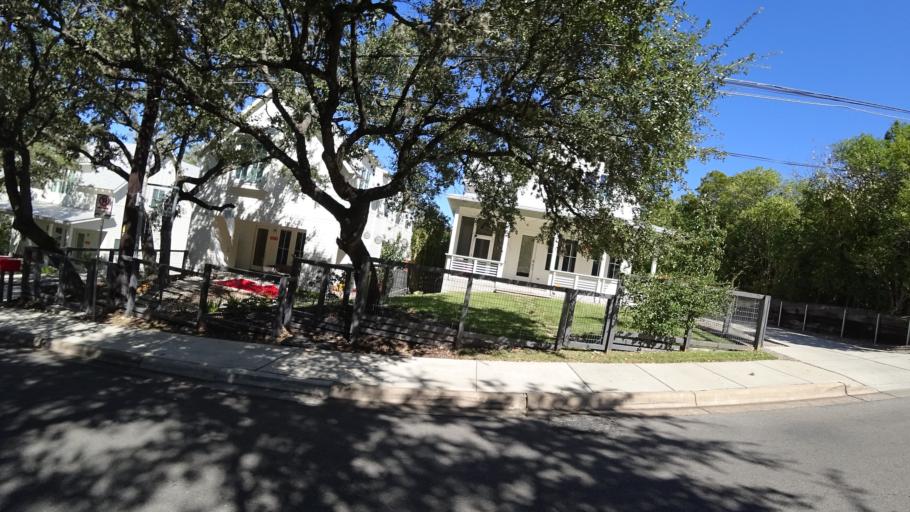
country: US
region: Texas
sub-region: Travis County
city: Austin
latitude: 30.2328
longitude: -97.7678
